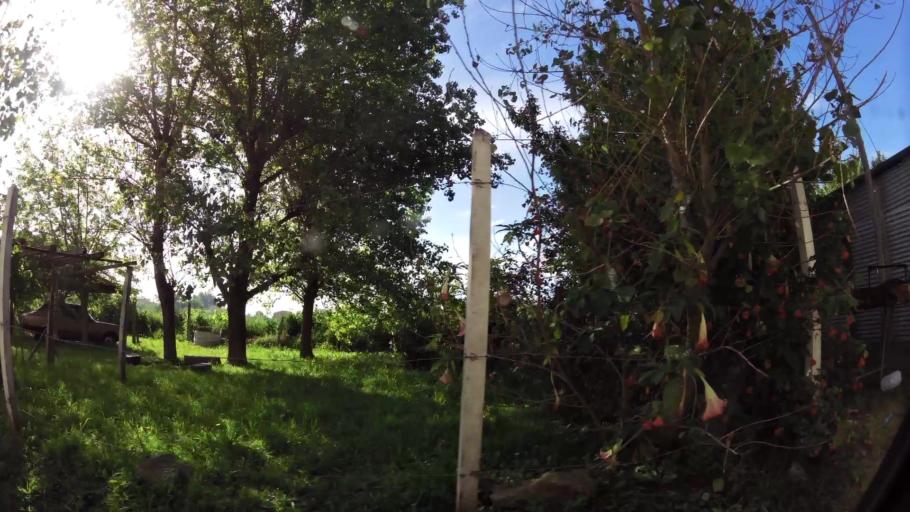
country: AR
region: Buenos Aires
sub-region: Partido de Quilmes
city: Quilmes
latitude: -34.7812
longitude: -58.2373
